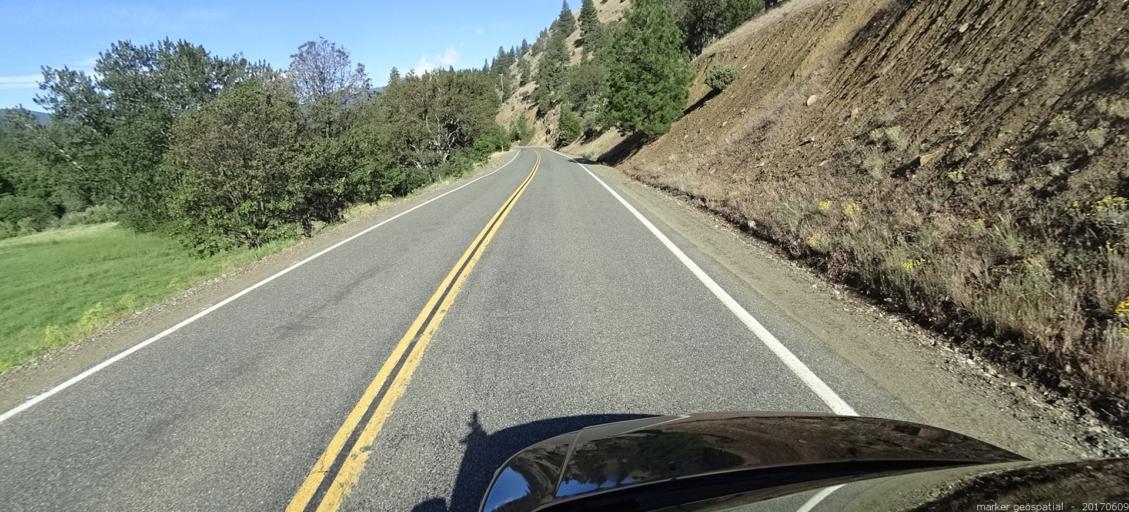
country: US
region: California
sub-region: Siskiyou County
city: Weed
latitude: 41.3118
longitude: -122.7593
